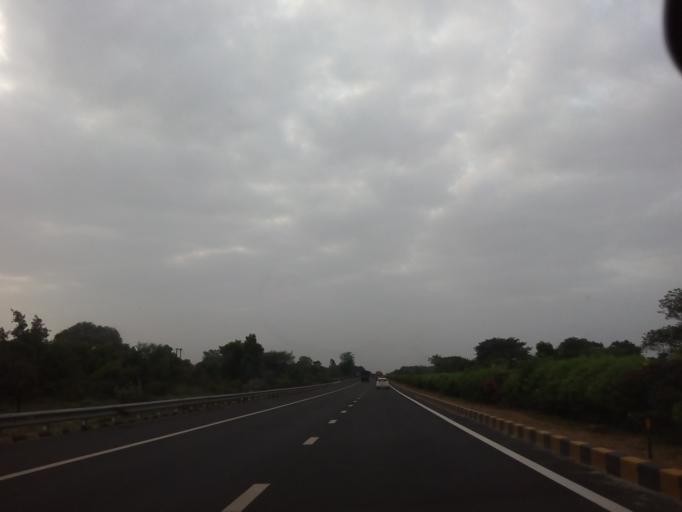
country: IN
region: Gujarat
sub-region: Kheda
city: Mahemdavad
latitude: 22.9283
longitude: 72.7374
